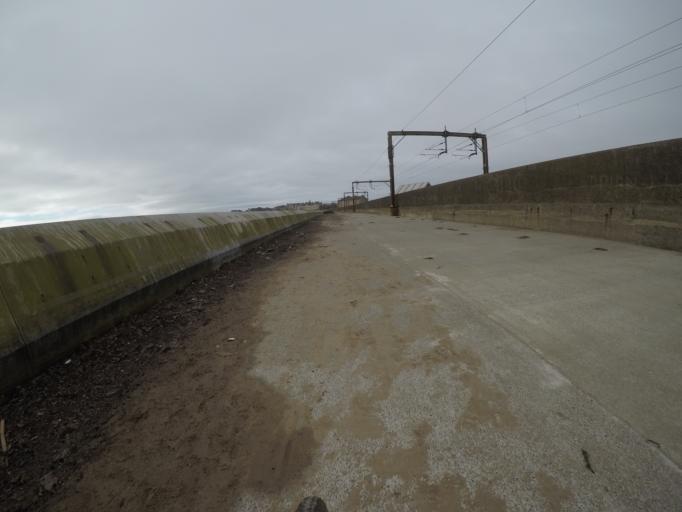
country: GB
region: Scotland
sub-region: North Ayrshire
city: Saltcoats
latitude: 55.6331
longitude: -4.7744
